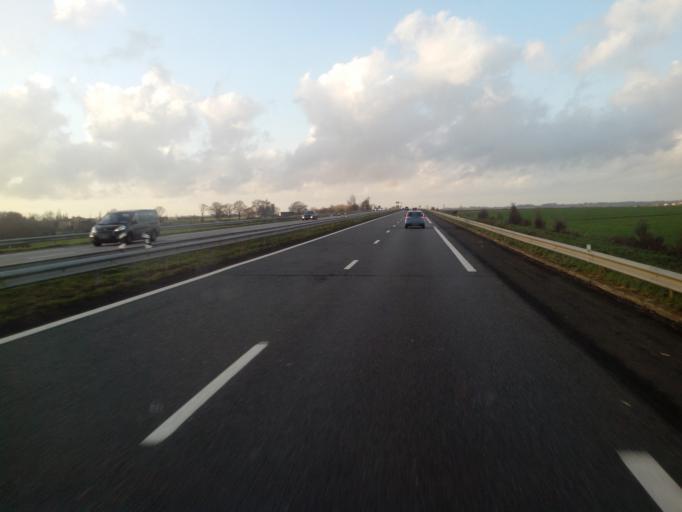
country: FR
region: Pays de la Loire
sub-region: Departement de Maine-et-Loire
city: Tillieres
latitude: 47.1349
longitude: -1.1544
